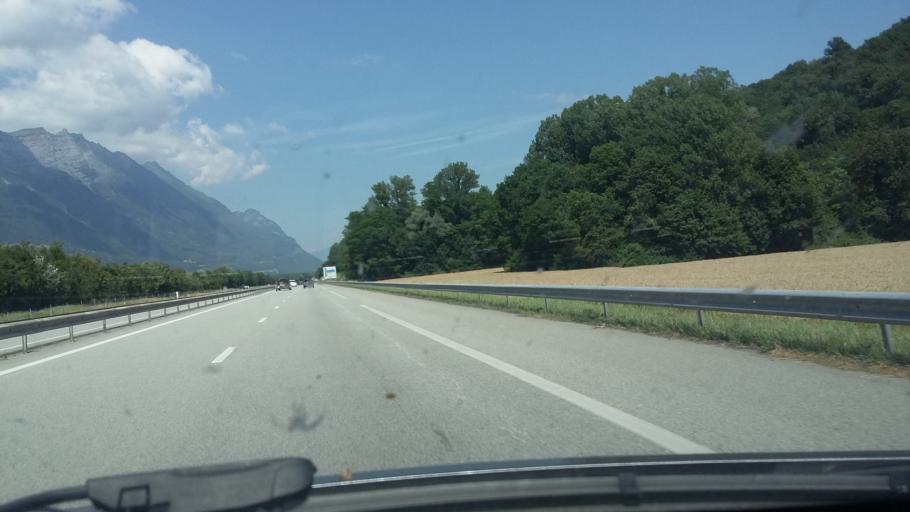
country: FR
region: Rhone-Alpes
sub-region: Departement de la Savoie
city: Coise-Saint-Jean-Pied-Gauthier
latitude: 45.5337
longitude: 6.1275
